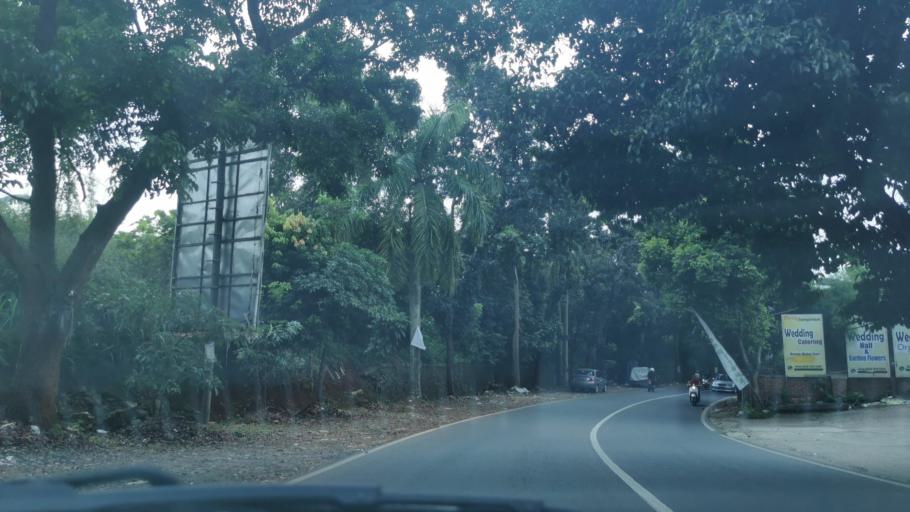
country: ID
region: West Java
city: Depok
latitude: -6.4095
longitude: 106.8317
